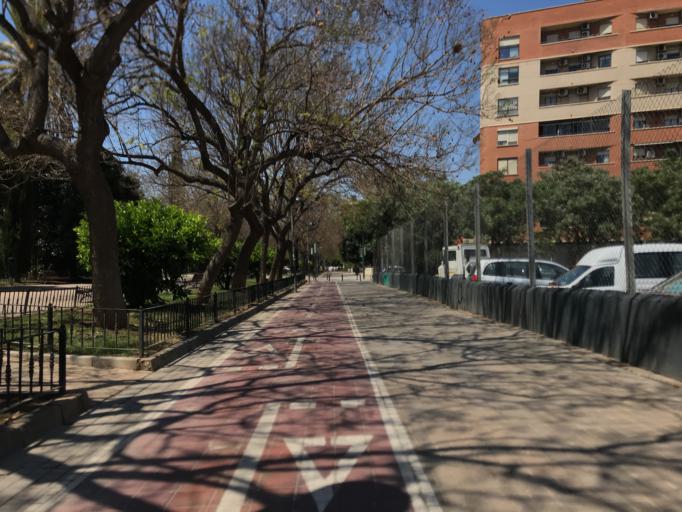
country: ES
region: Valencia
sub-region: Provincia de Valencia
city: Mislata
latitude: 39.4598
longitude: -0.4029
